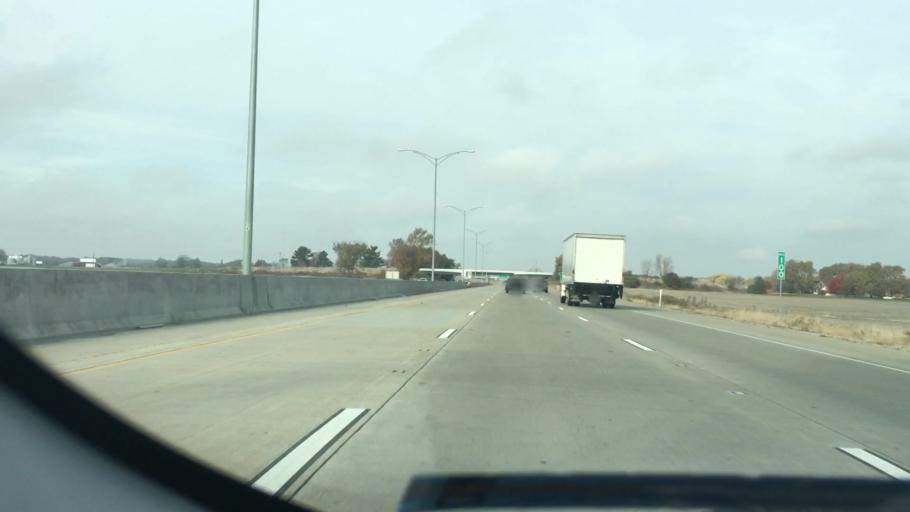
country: US
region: Illinois
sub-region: Tazewell County
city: Morton
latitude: 40.6276
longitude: -89.5030
